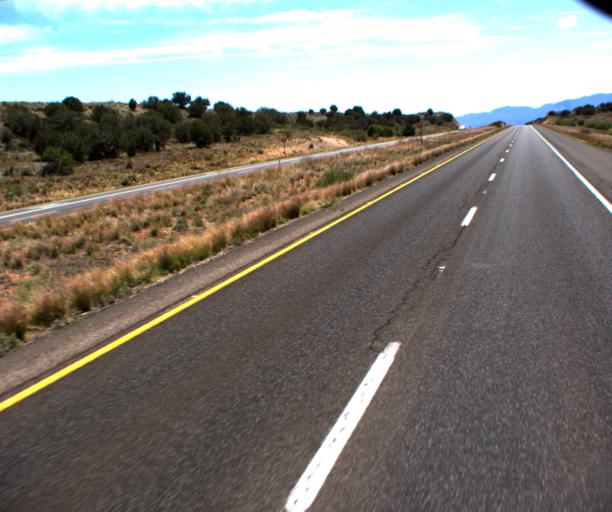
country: US
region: Arizona
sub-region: Yavapai County
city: Cornville
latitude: 34.8092
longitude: -111.9084
